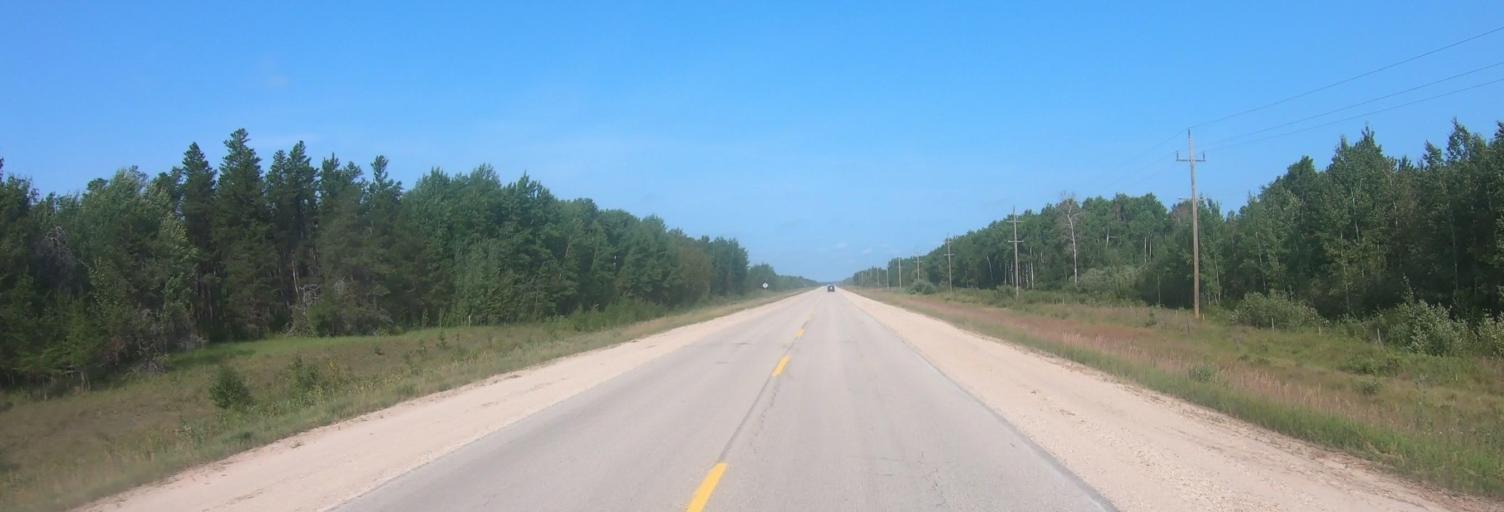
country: US
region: Minnesota
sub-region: Roseau County
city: Roseau
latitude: 49.1410
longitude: -96.1056
